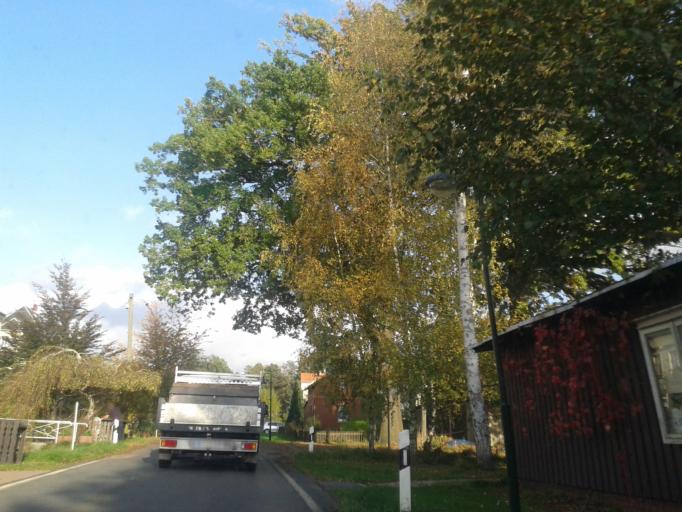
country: DE
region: Saxony
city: Wilsdruff
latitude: 51.0265
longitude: 13.4661
